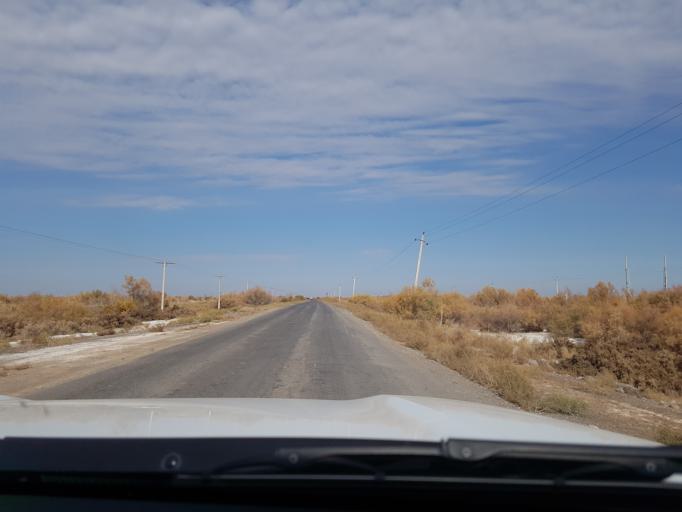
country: TM
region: Ahal
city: Tejen
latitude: 37.3600
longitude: 61.0927
